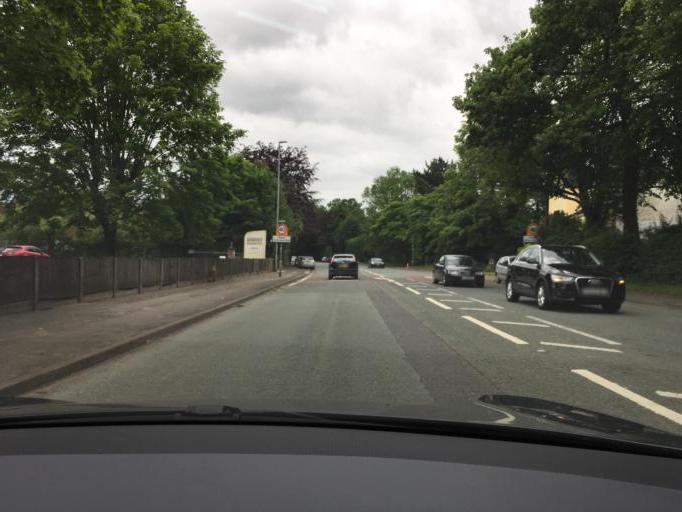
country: GB
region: England
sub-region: Cheshire East
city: Poynton
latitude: 53.3405
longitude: -2.1279
